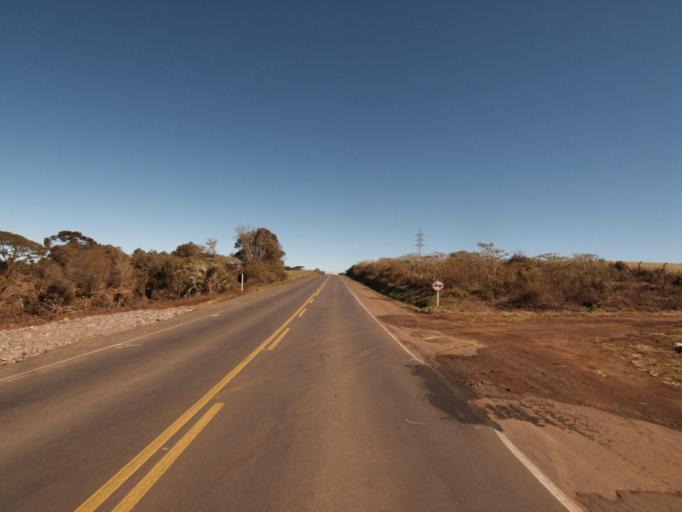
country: BR
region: Santa Catarina
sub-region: Concordia
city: Concordia
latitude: -26.9164
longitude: -51.9227
